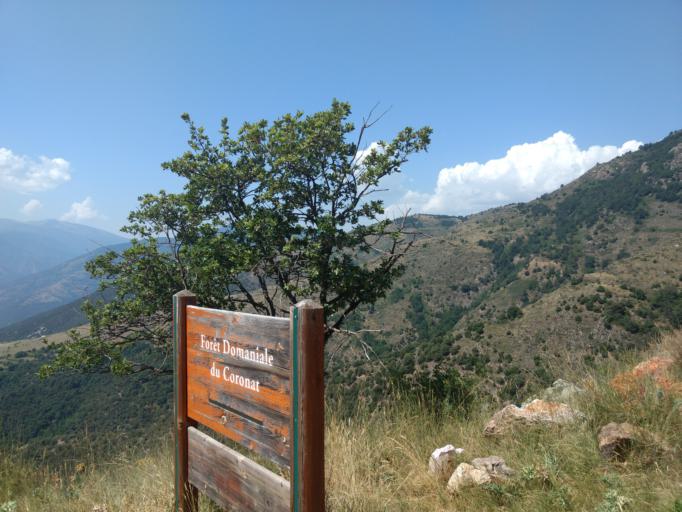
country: FR
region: Languedoc-Roussillon
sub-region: Departement des Pyrenees-Orientales
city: Vernet-les-Bains
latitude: 42.5822
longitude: 2.3005
